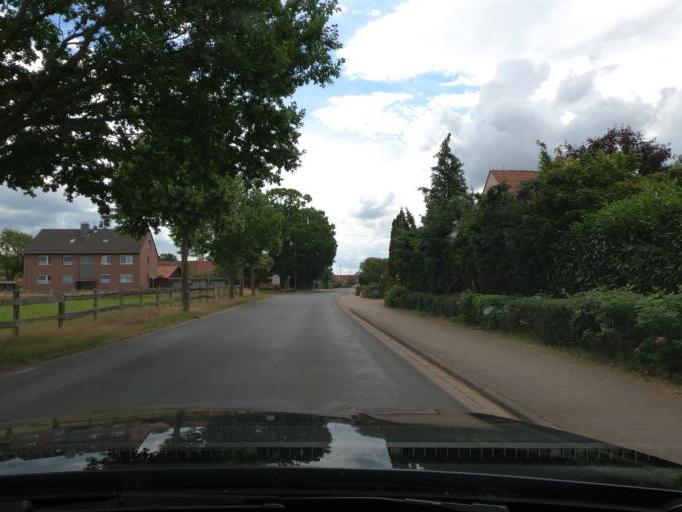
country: DE
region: Lower Saxony
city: Sehnde
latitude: 52.3420
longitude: 9.9108
